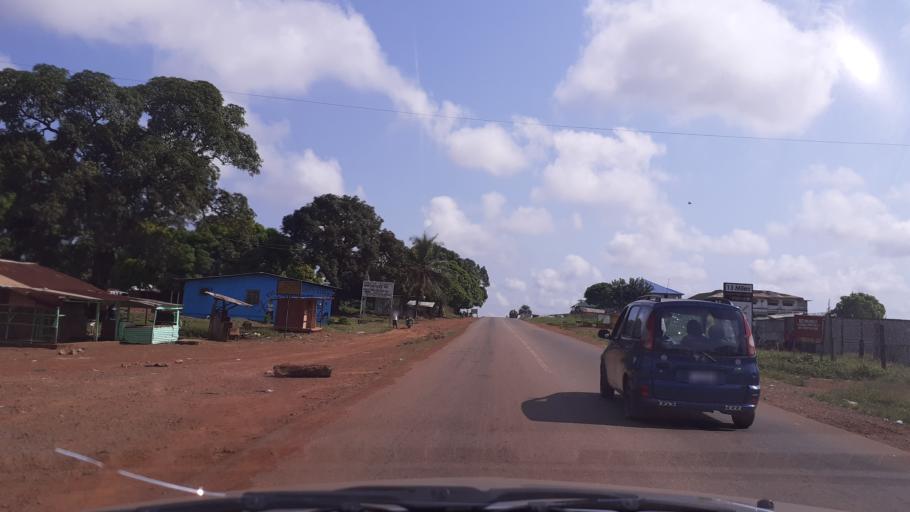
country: LR
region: Montserrado
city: Bensonville City
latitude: 6.2243
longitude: -10.5353
